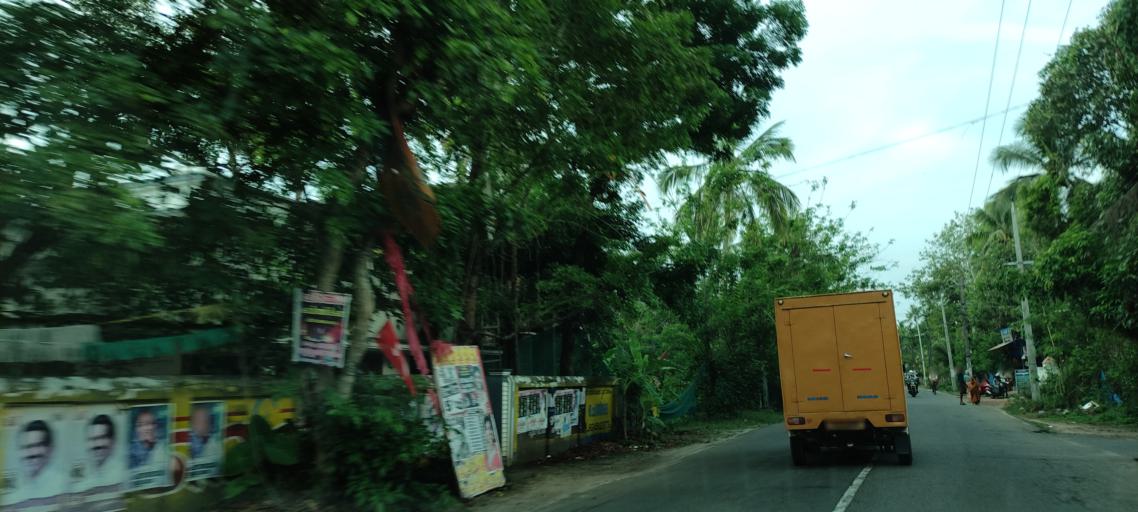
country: IN
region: Kerala
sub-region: Kottayam
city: Vaikam
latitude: 9.7606
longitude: 76.3625
